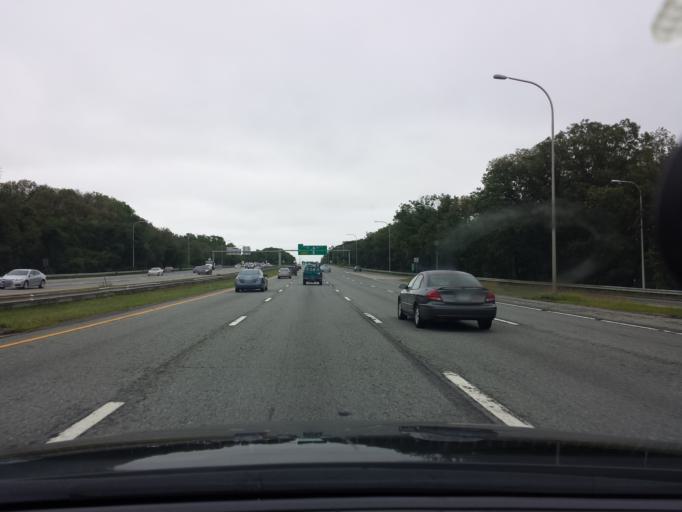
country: US
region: Rhode Island
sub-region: Kent County
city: East Greenwich
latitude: 41.6996
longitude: -71.4745
